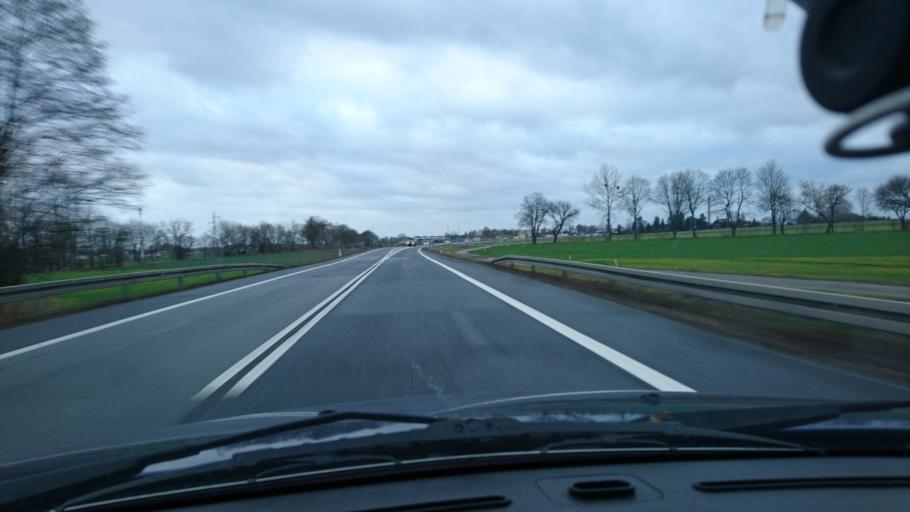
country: PL
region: Opole Voivodeship
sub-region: Powiat kluczborski
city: Kluczbork
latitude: 50.9910
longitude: 18.2183
